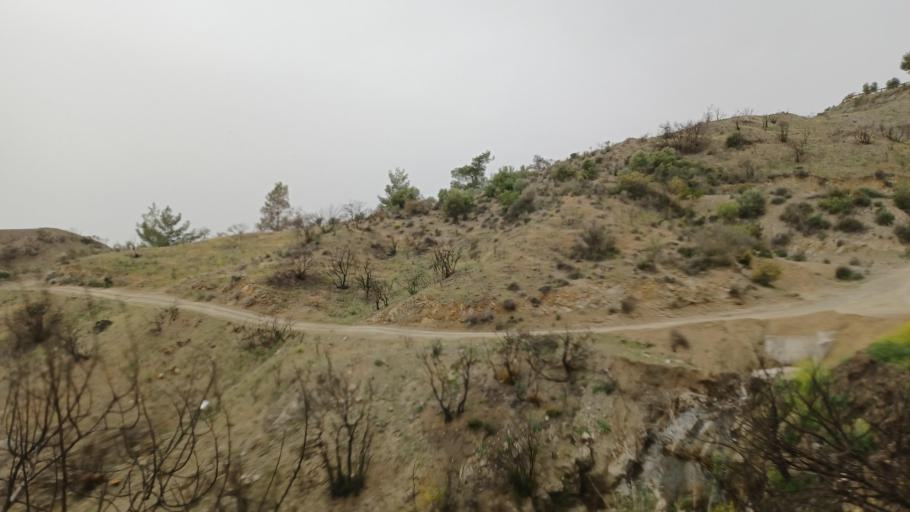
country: CY
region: Limassol
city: Parekklisha
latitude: 34.8532
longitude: 33.1371
